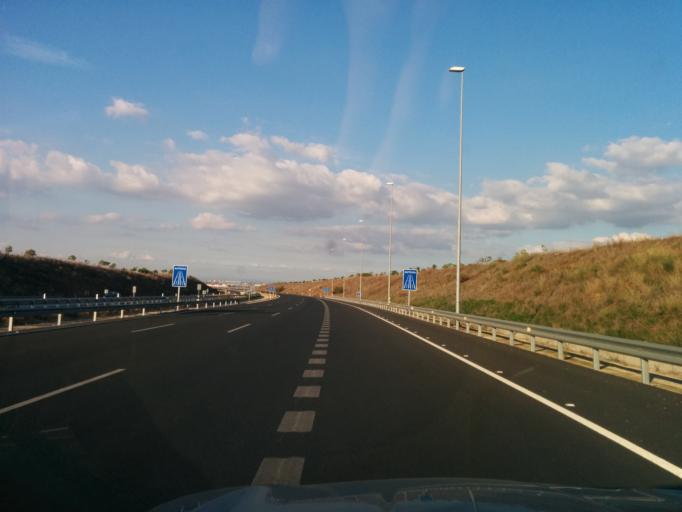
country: ES
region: Andalusia
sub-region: Provincia de Sevilla
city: Dos Hermanas
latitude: 37.3236
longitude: -5.8913
